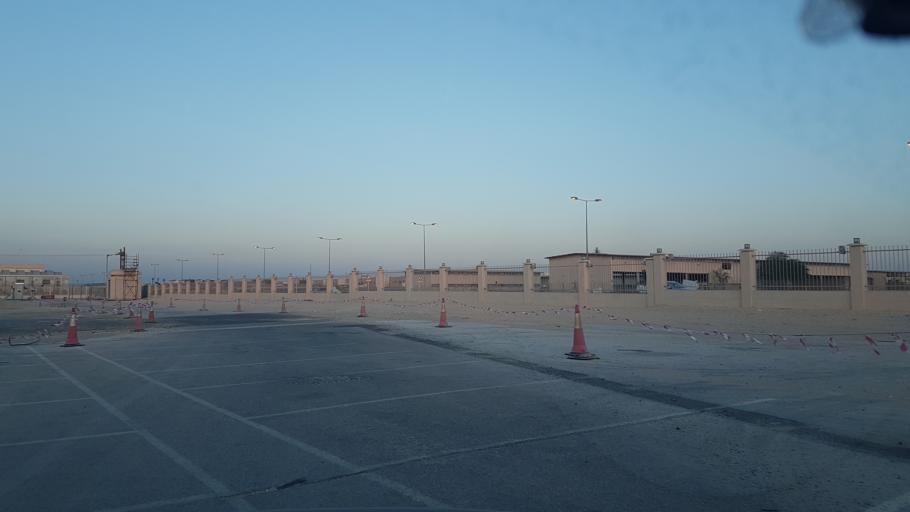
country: BH
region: Northern
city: Ar Rifa'
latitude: 26.0905
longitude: 50.5523
